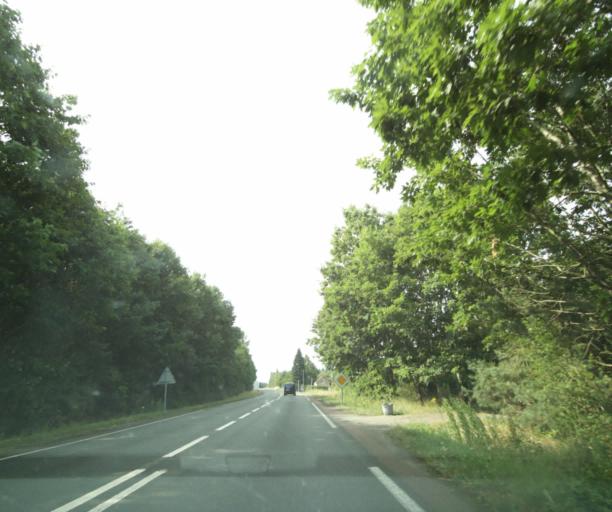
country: FR
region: Pays de la Loire
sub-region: Departement de la Sarthe
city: Marigne-Laille
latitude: 47.7757
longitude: 0.3448
